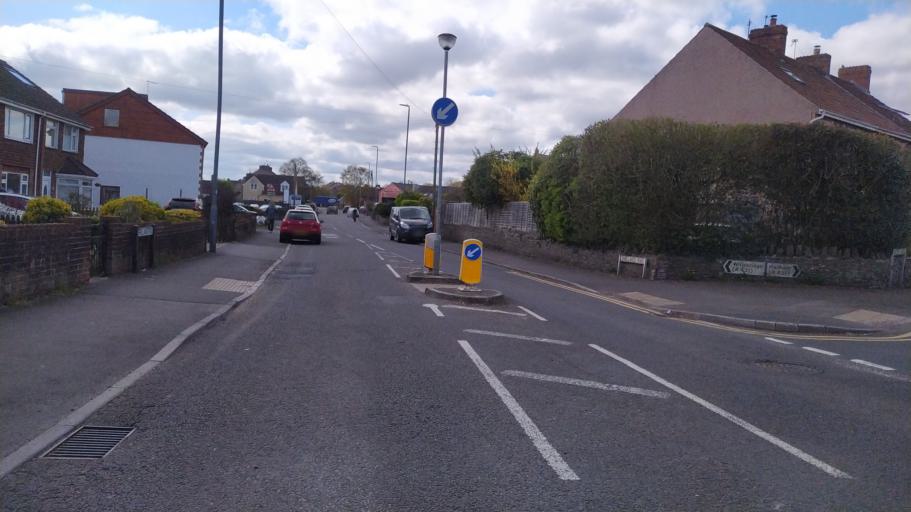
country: GB
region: England
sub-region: South Gloucestershire
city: Kingswood
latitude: 51.4398
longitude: -2.4928
